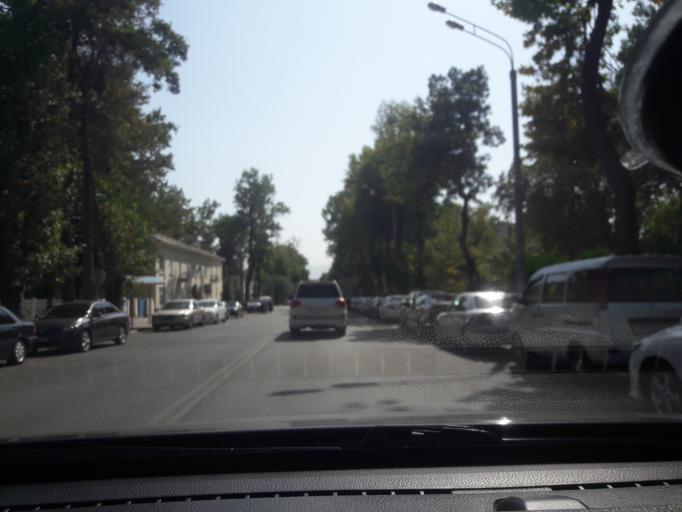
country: TJ
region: Dushanbe
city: Dushanbe
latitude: 38.5707
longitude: 68.7999
